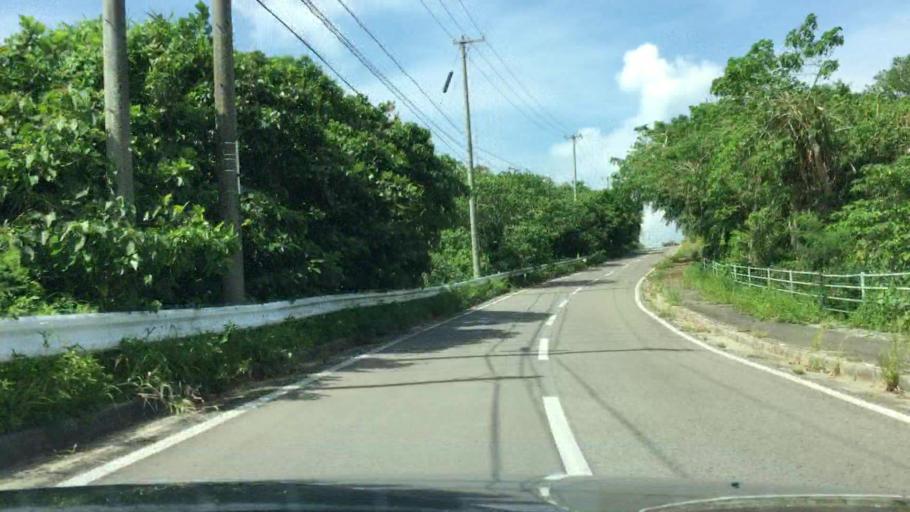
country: JP
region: Okinawa
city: Ishigaki
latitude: 24.4888
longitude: 124.2316
